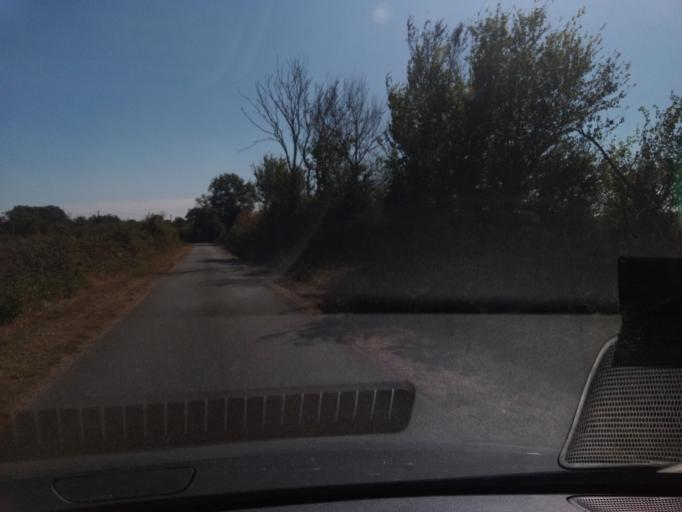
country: FR
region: Poitou-Charentes
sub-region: Departement de la Vienne
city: Lussac-les-Chateaux
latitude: 46.3978
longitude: 0.7480
